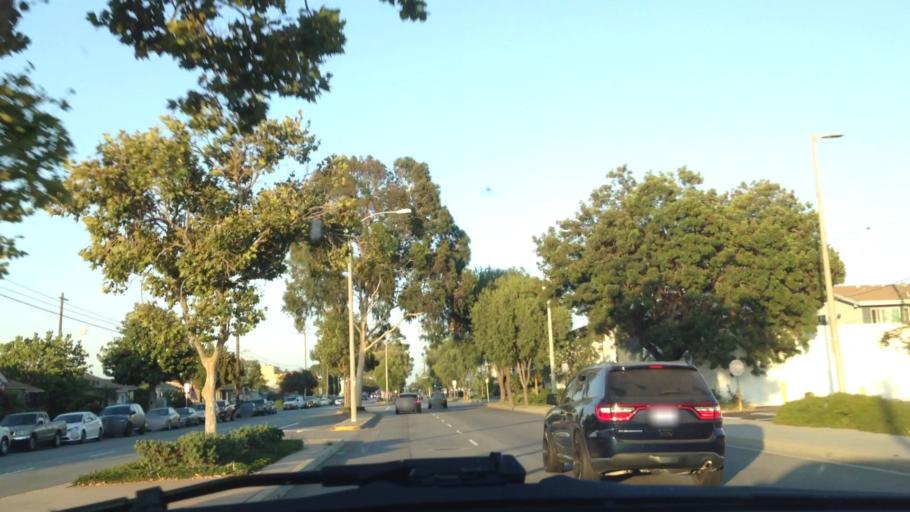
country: US
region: California
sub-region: Los Angeles County
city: Norwalk
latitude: 33.8875
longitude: -118.0900
